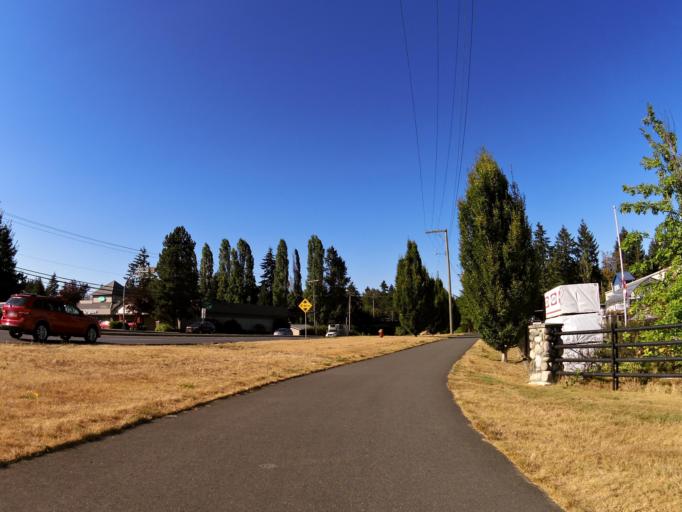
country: CA
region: British Columbia
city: Nanaimo
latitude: 49.1314
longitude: -123.9211
